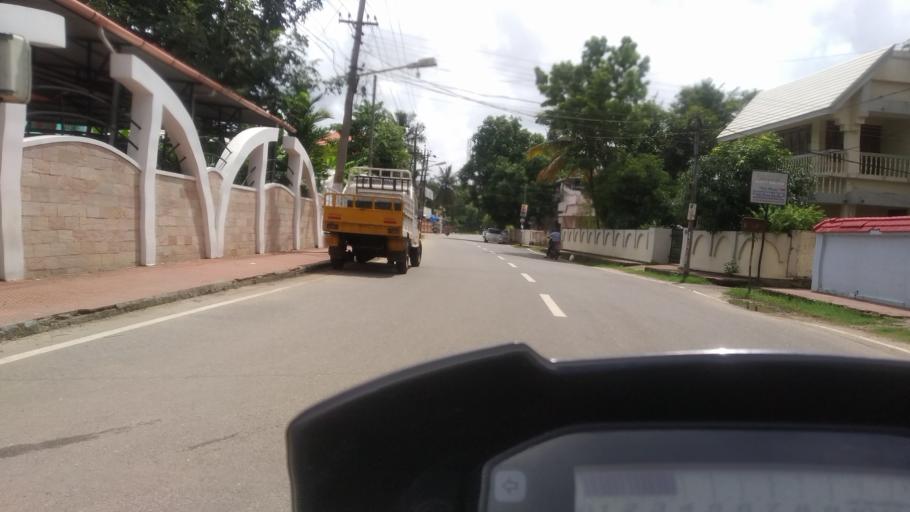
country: IN
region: Kerala
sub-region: Ernakulam
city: Aluva
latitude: 10.1190
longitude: 76.3456
